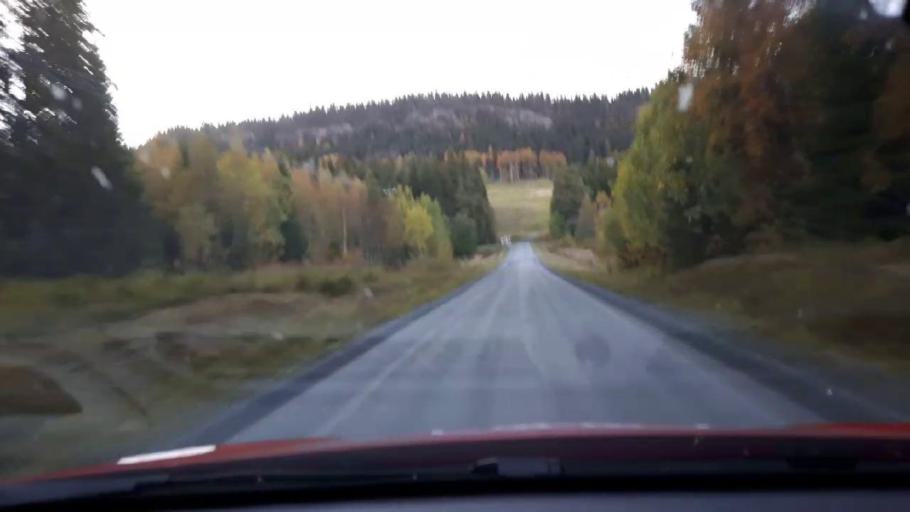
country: SE
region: Jaemtland
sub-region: Krokoms Kommun
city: Krokom
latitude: 63.4860
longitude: 14.2030
